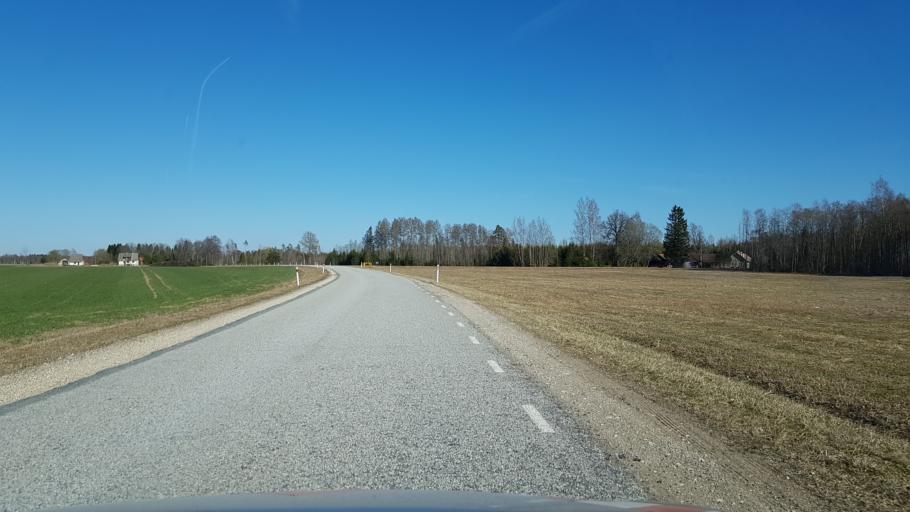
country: EE
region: Ida-Virumaa
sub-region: Aseri vald
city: Aseri
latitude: 59.2294
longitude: 26.7205
